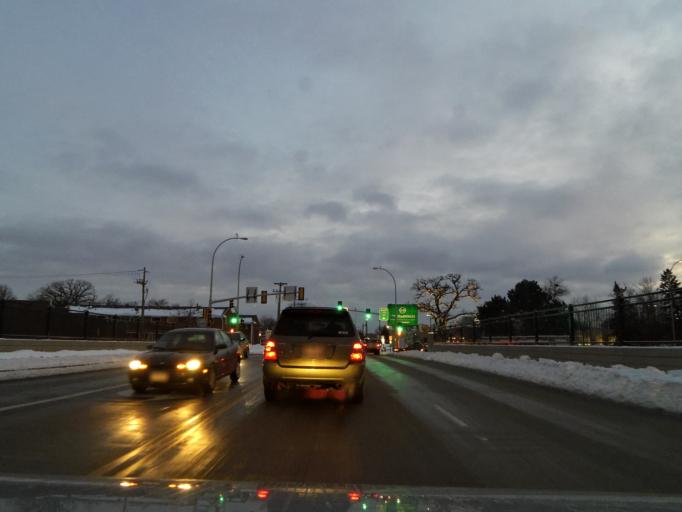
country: US
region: Minnesota
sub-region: Hennepin County
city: Richfield
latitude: 44.8909
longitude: -93.3087
